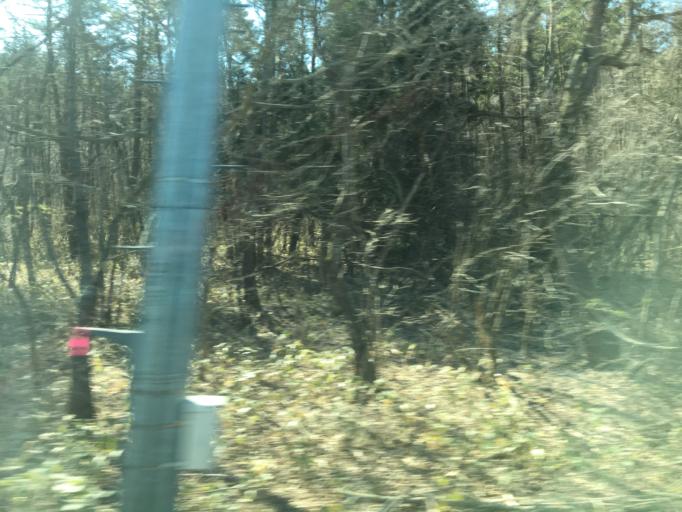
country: JP
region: Aomori
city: Hachinohe
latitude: 40.2807
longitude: 141.7787
